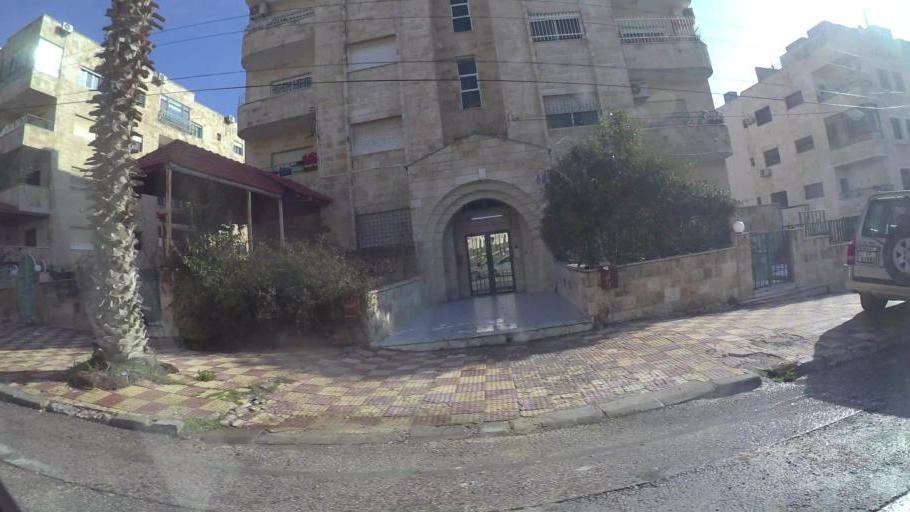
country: JO
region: Amman
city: Al Jubayhah
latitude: 32.0032
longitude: 35.8532
